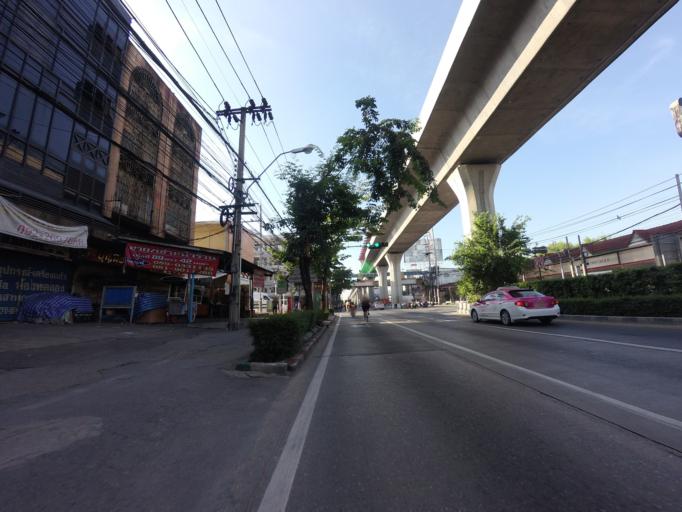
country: TH
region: Bangkok
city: Bang Na
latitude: 13.6589
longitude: 100.6011
